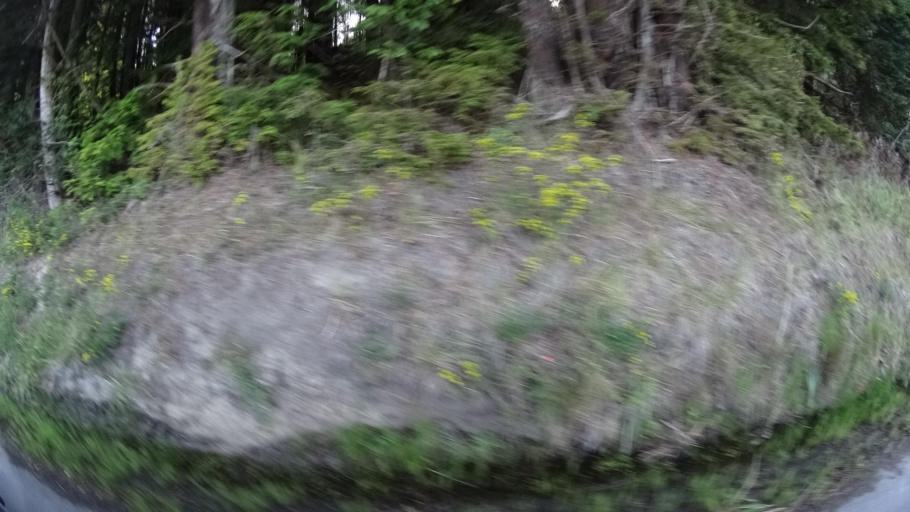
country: US
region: California
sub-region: Humboldt County
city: Myrtletown
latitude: 40.7821
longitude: -124.1183
